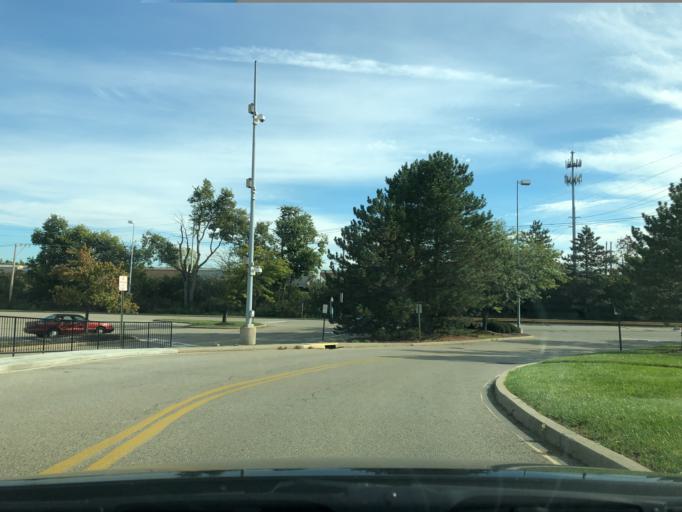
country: US
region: Ohio
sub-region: Hamilton County
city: Glendale
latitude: 39.2920
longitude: -84.4634
